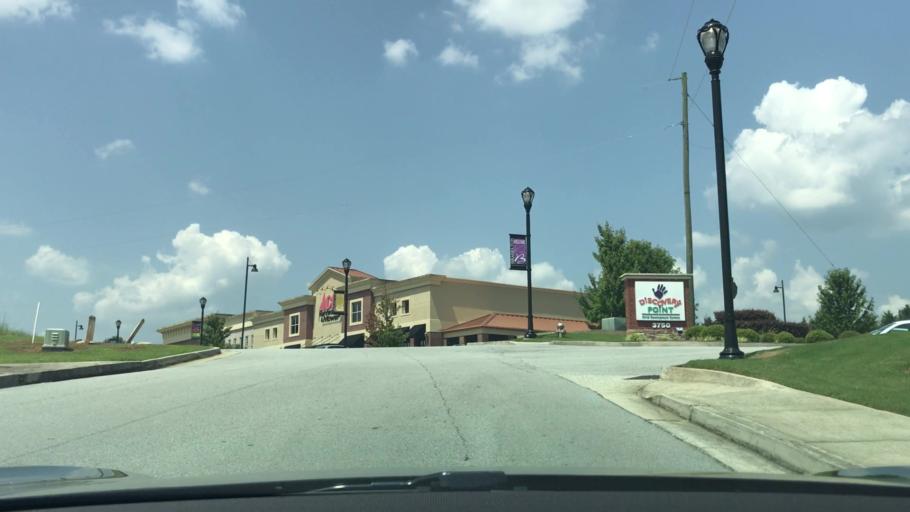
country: US
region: Georgia
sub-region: Jackson County
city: Braselton
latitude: 34.1138
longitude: -83.8180
